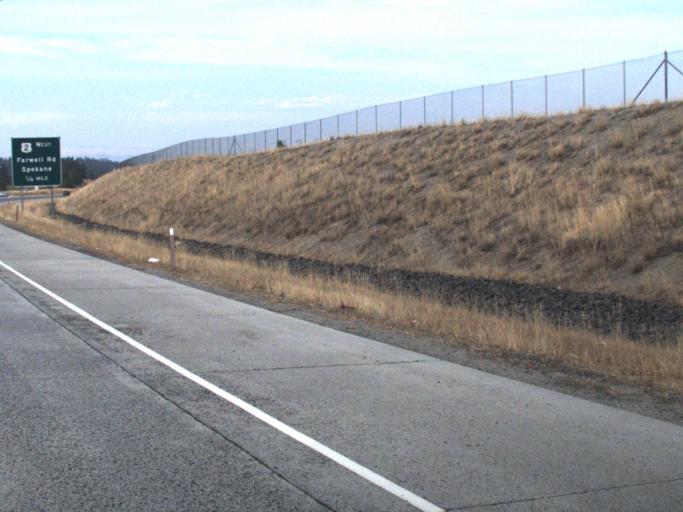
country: US
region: Washington
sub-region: Spokane County
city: Mead
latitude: 47.7603
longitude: -117.3656
